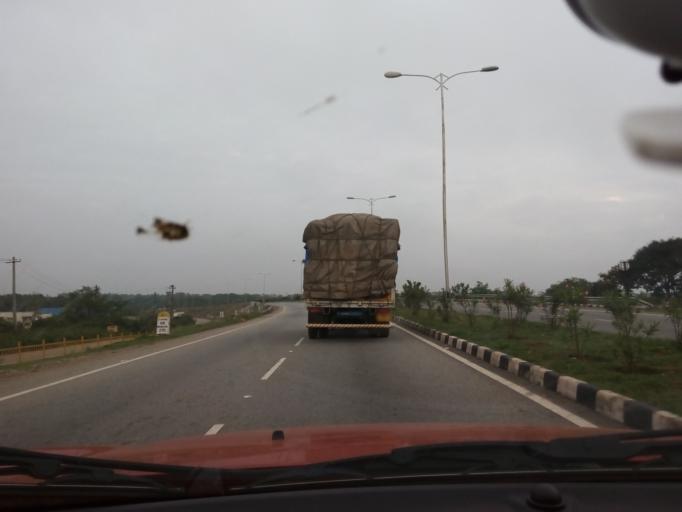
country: IN
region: Karnataka
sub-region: Tumkur
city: Kunigal
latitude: 13.0030
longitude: 76.9566
